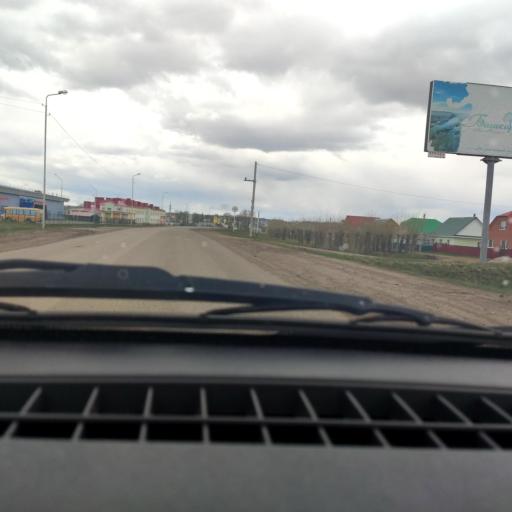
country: RU
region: Bashkortostan
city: Chekmagush
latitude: 55.1316
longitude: 54.6790
